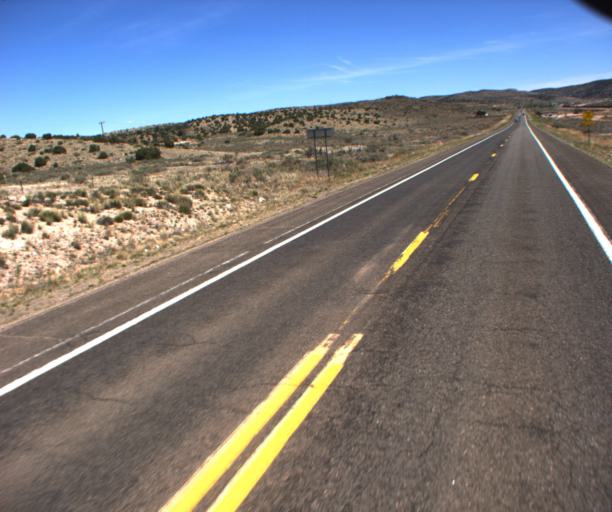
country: US
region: Arizona
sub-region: Mohave County
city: Peach Springs
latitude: 35.5230
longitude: -113.4470
